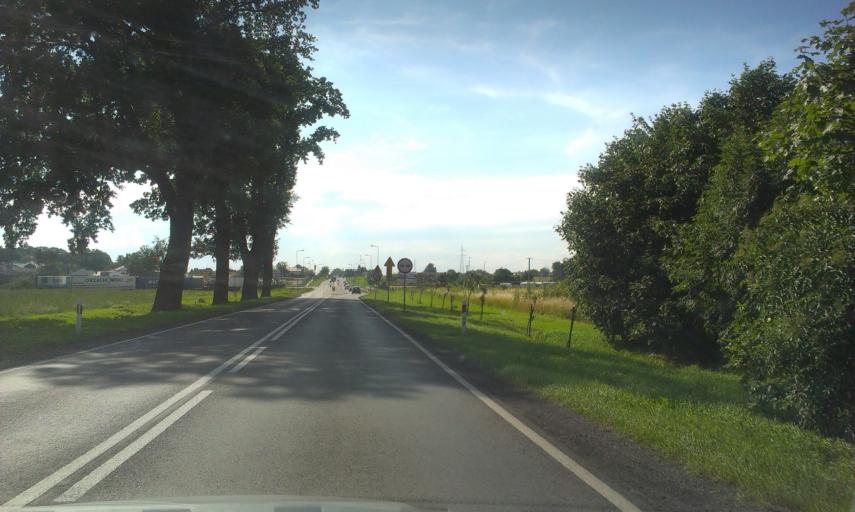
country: PL
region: Kujawsko-Pomorskie
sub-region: Powiat bydgoski
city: Sicienko
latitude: 53.1577
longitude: 17.8537
